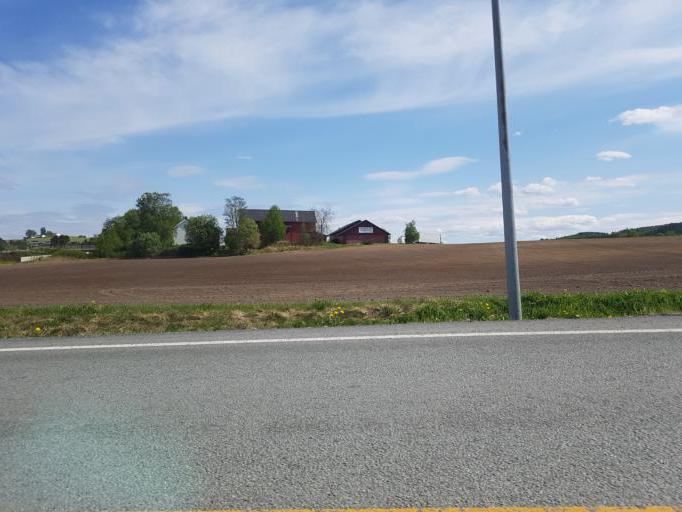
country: NO
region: Nord-Trondelag
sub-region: Levanger
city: Levanger
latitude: 63.7312
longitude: 11.2930
